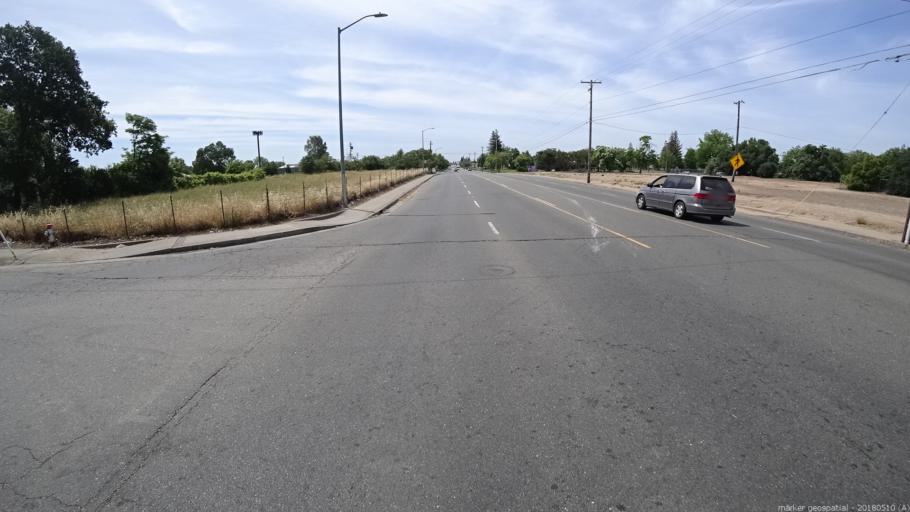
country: US
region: California
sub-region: Sacramento County
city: Rio Linda
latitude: 38.6328
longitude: -121.4569
